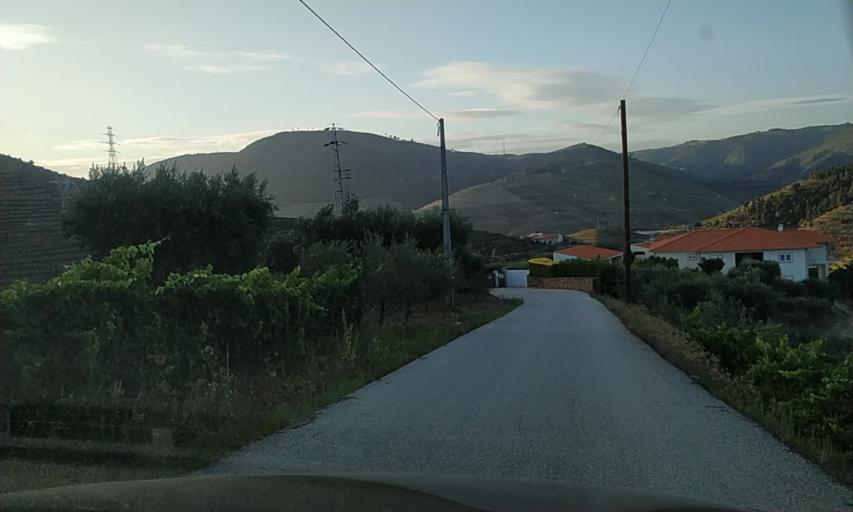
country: PT
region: Viseu
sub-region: Armamar
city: Armamar
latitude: 41.1300
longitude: -7.6947
